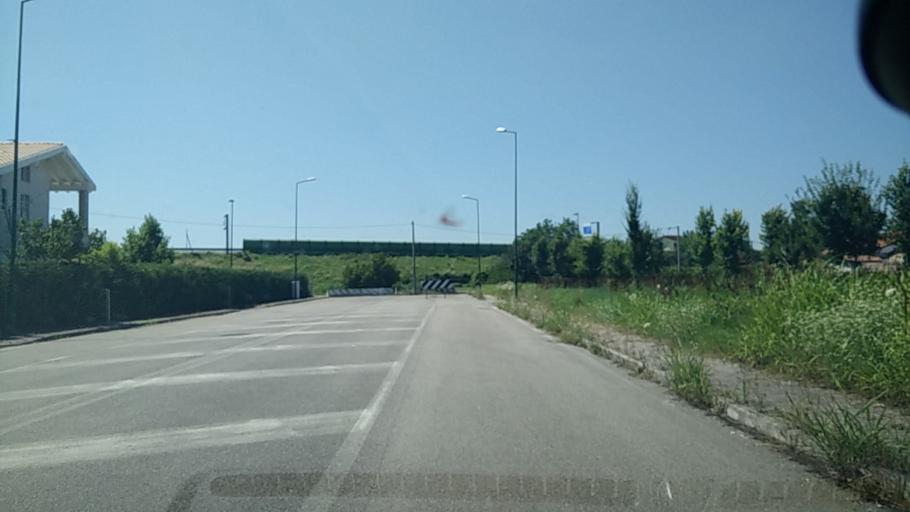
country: IT
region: Veneto
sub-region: Provincia di Venezia
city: Dese
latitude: 45.5363
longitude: 12.2945
